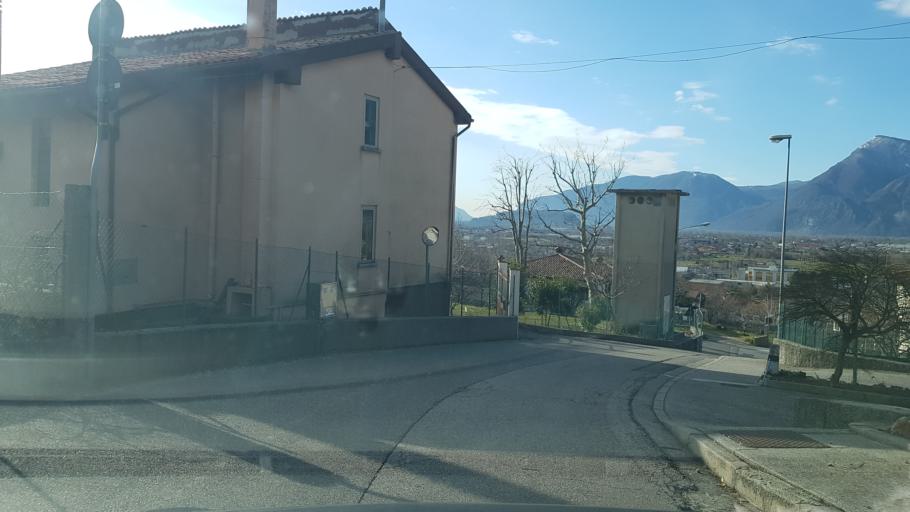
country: IT
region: Friuli Venezia Giulia
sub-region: Provincia di Udine
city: Gemona
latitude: 46.2863
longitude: 13.1328
